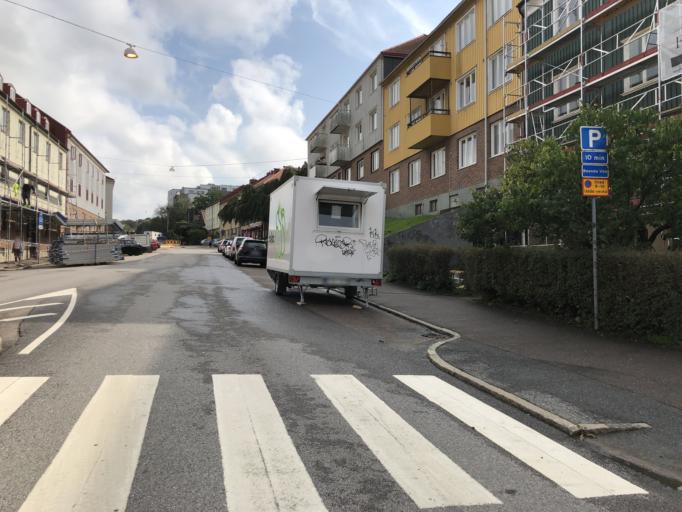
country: SE
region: Vaestra Goetaland
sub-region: Goteborg
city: Majorna
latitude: 57.6910
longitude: 11.9299
